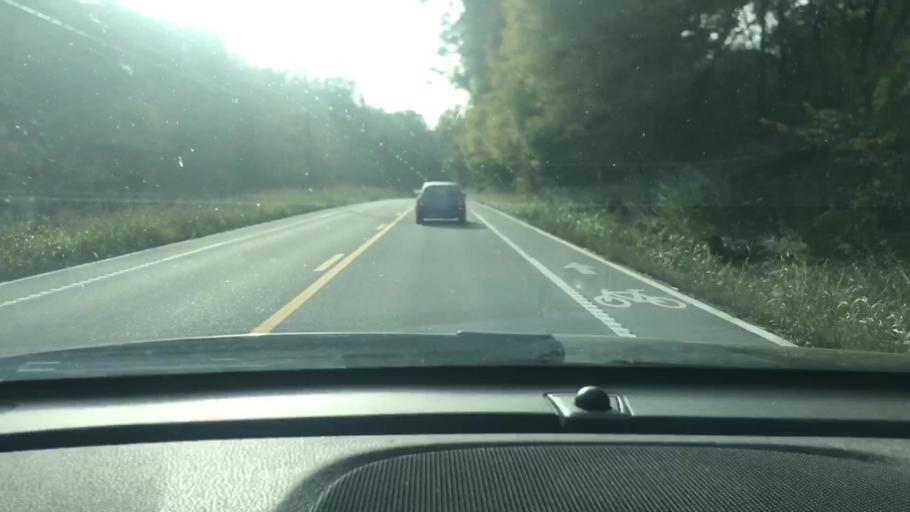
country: US
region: Tennessee
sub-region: Cheatham County
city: Pegram
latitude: 36.0143
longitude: -87.0407
